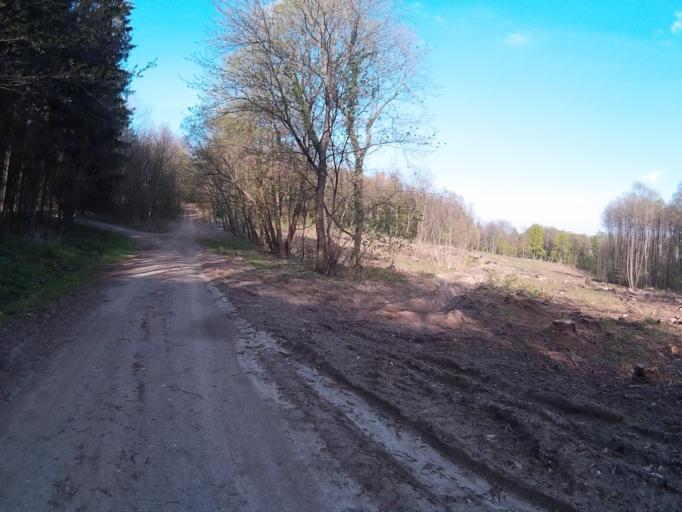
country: AT
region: Burgenland
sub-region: Politischer Bezirk Oberwart
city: Rechnitz
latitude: 47.3387
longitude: 16.4806
